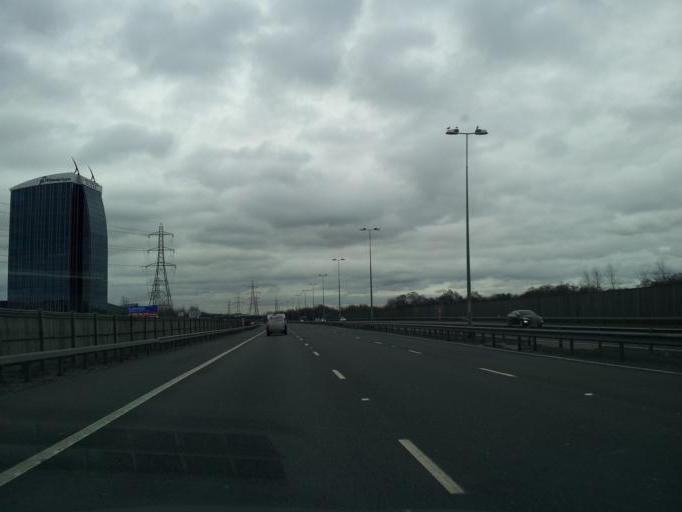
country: GB
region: England
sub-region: Staffordshire
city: Cannock
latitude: 52.6711
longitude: -2.0356
